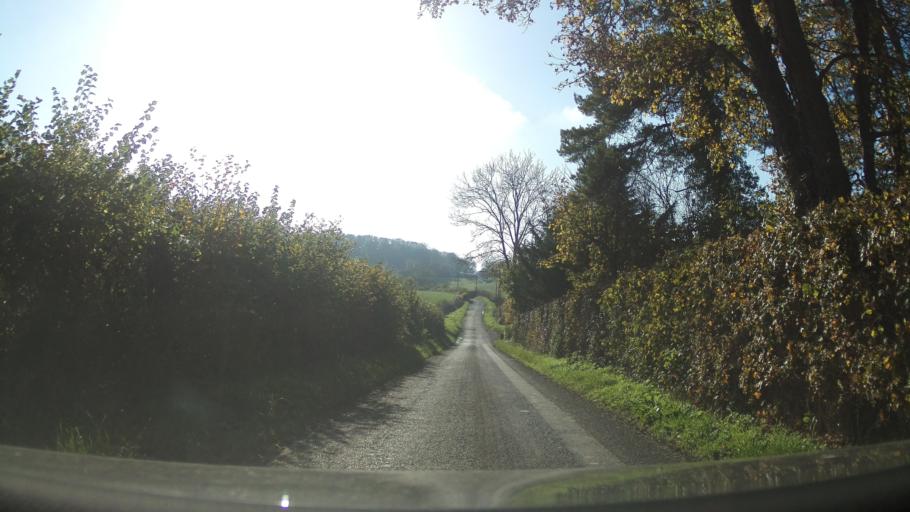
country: GB
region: England
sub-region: Somerset
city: Castle Cary
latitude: 51.0648
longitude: -2.4768
